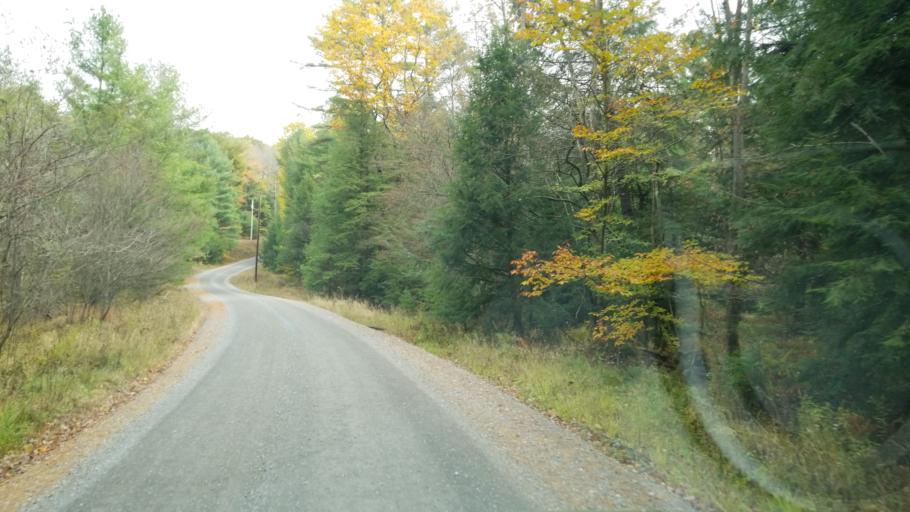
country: US
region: Pennsylvania
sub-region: Clearfield County
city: Clearfield
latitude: 41.1961
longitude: -78.4078
